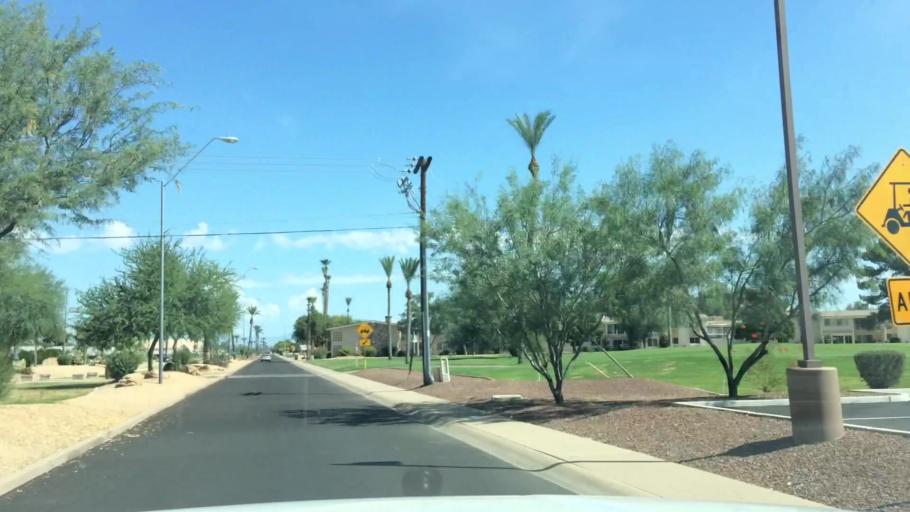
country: US
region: Arizona
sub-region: Maricopa County
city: Youngtown
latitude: 33.5813
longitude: -112.2899
